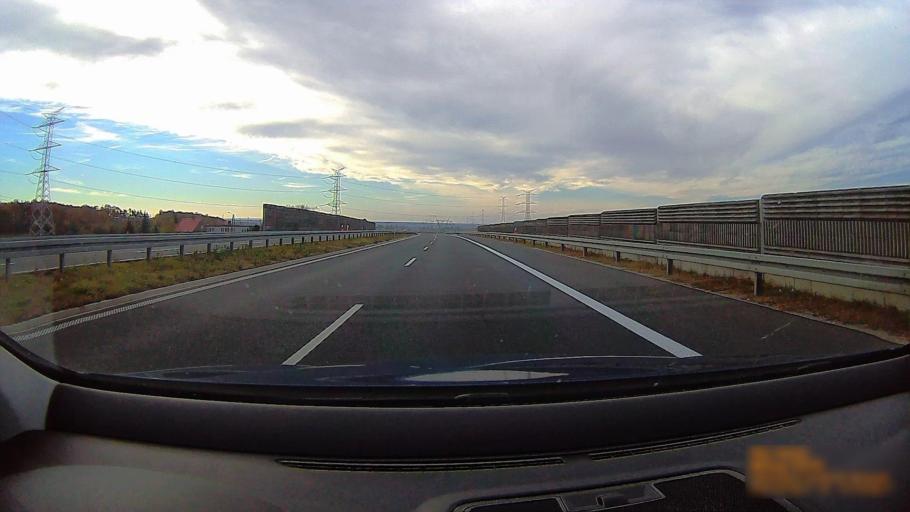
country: PL
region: Greater Poland Voivodeship
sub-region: Powiat ostrowski
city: Przygodzice
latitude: 51.6215
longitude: 17.8626
